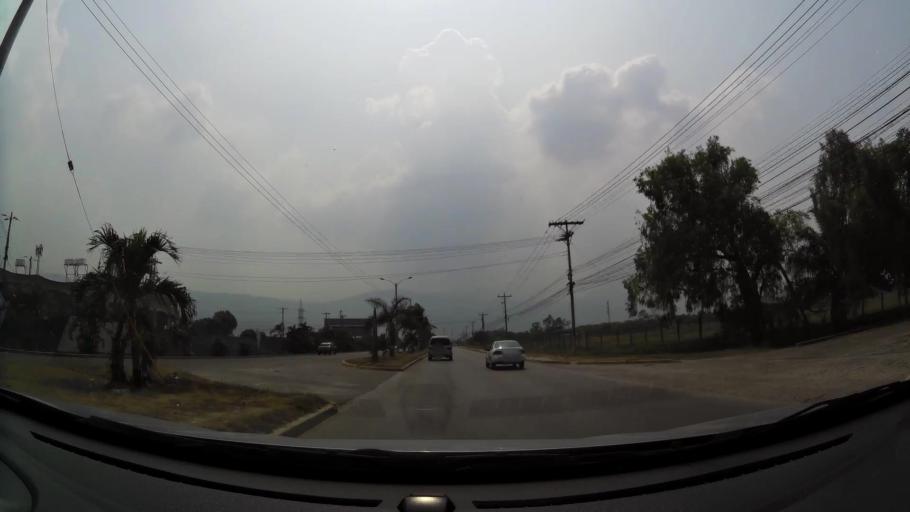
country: HN
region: Cortes
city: San Pedro Sula
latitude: 15.4720
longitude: -88.0057
